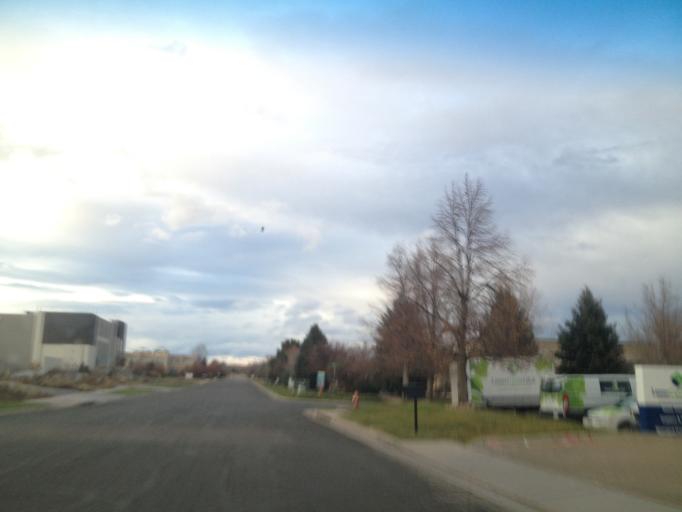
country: US
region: Colorado
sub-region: Boulder County
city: Louisville
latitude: 39.9623
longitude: -105.1196
